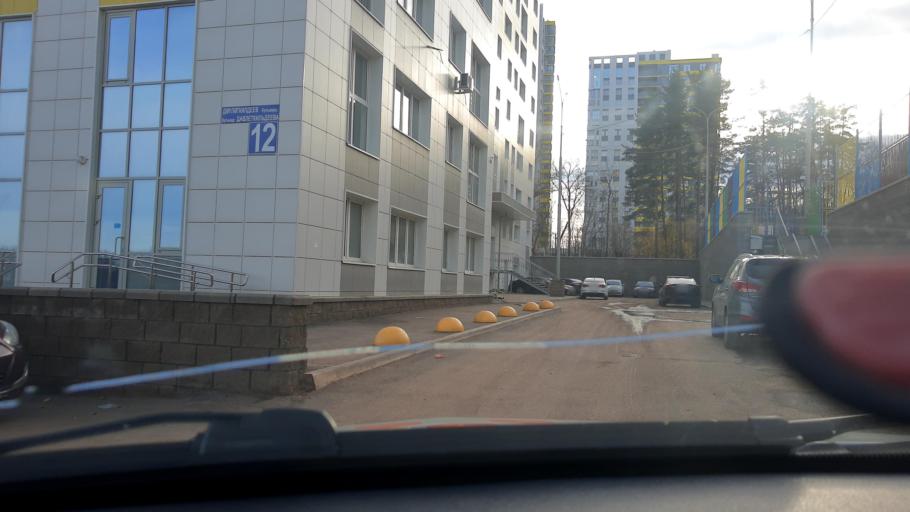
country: RU
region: Bashkortostan
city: Ufa
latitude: 54.7649
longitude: 56.0328
